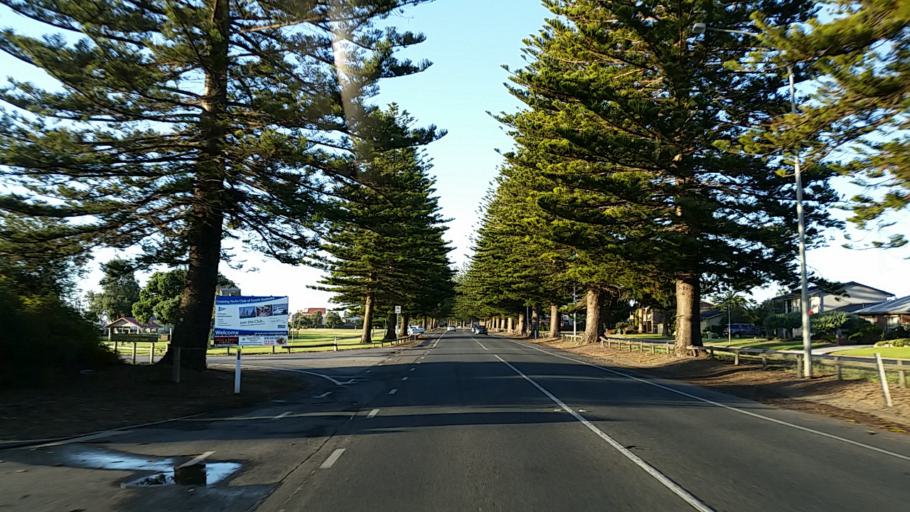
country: AU
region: South Australia
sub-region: Port Adelaide Enfield
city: Birkenhead
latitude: -34.7950
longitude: 138.4915
